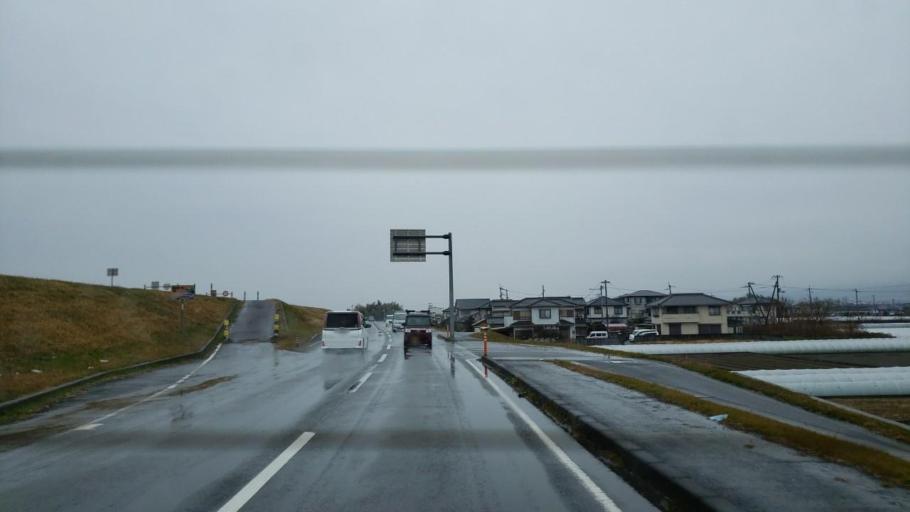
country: JP
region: Tokushima
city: Ishii
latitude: 34.1077
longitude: 134.4321
